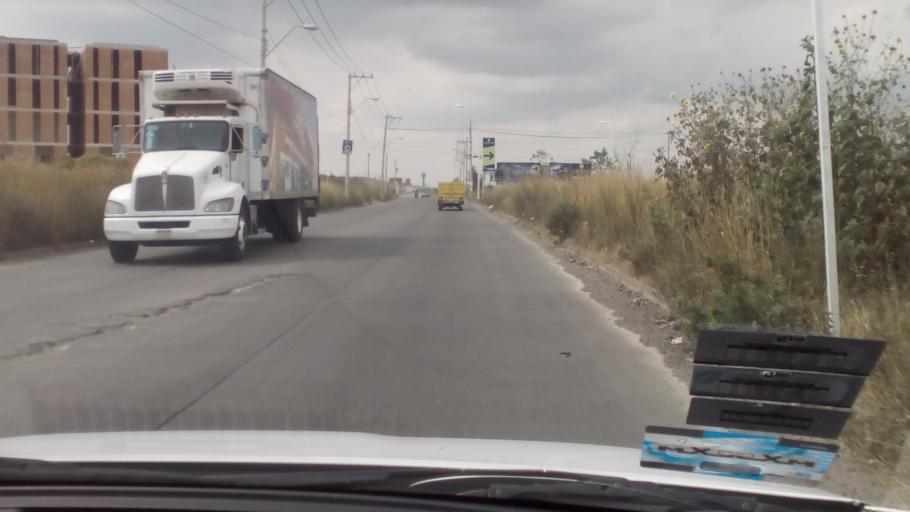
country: MX
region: Guanajuato
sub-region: Leon
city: Fraccionamiento Paseo de las Torres
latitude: 21.1716
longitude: -101.7516
